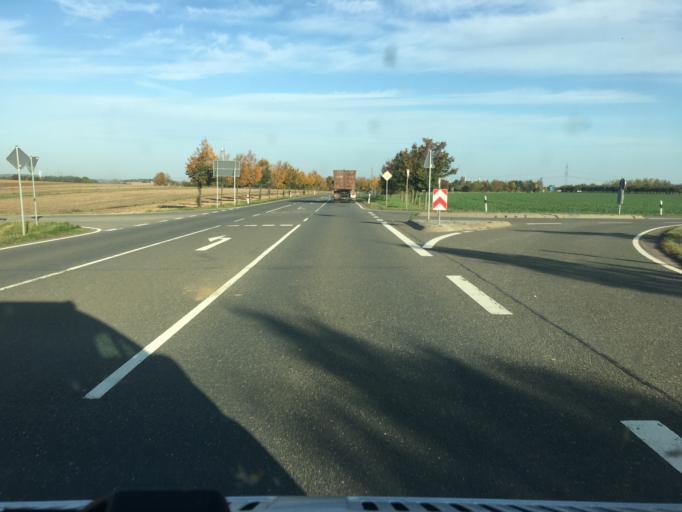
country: DE
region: Thuringia
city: Heyersdorf
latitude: 50.8418
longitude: 12.3363
